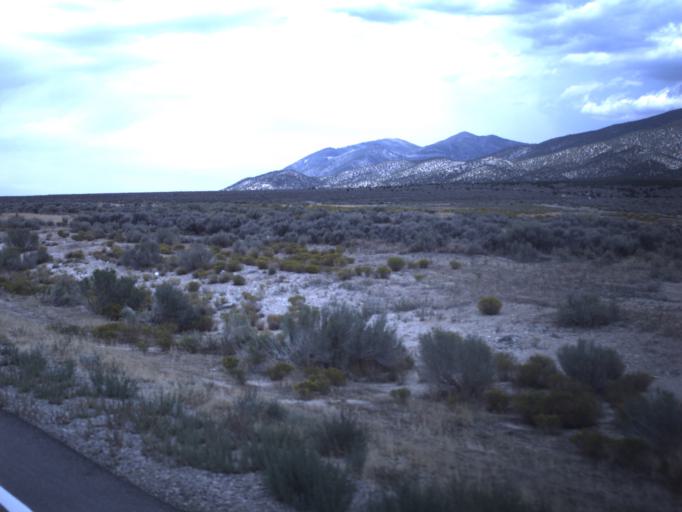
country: US
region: Utah
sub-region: Tooele County
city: Tooele
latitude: 40.2851
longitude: -112.2635
